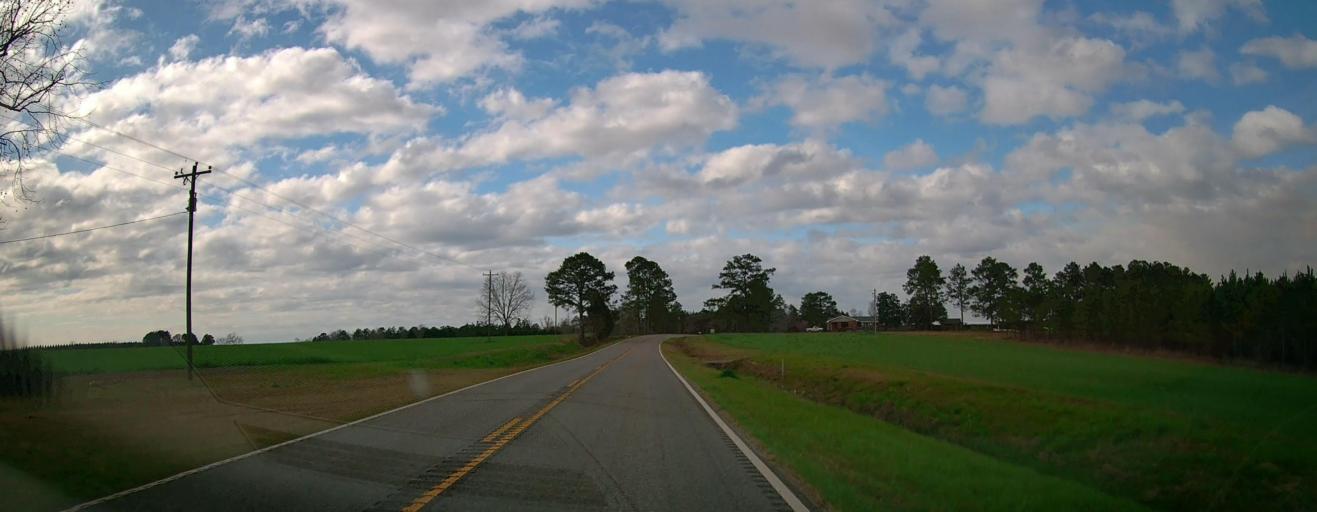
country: US
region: Georgia
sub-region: Marion County
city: Buena Vista
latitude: 32.4420
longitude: -84.4385
